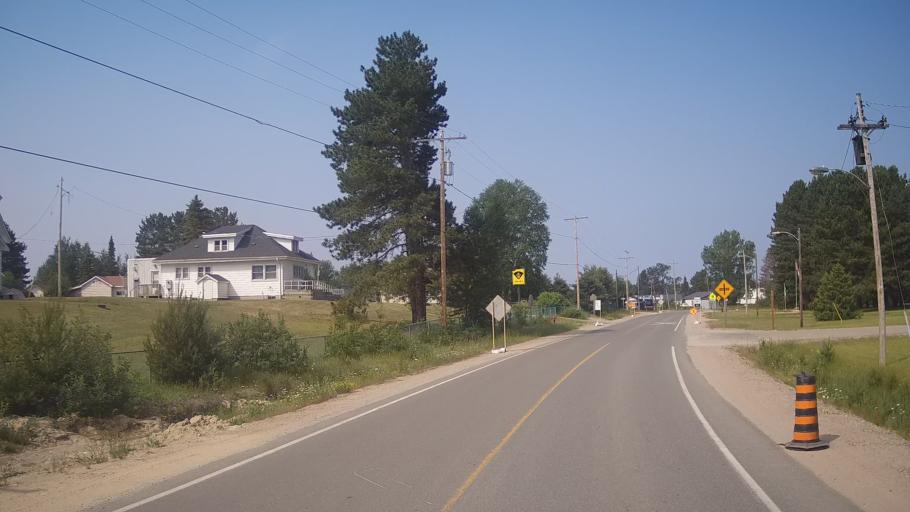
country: CA
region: Ontario
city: Timmins
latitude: 47.6756
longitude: -81.7201
